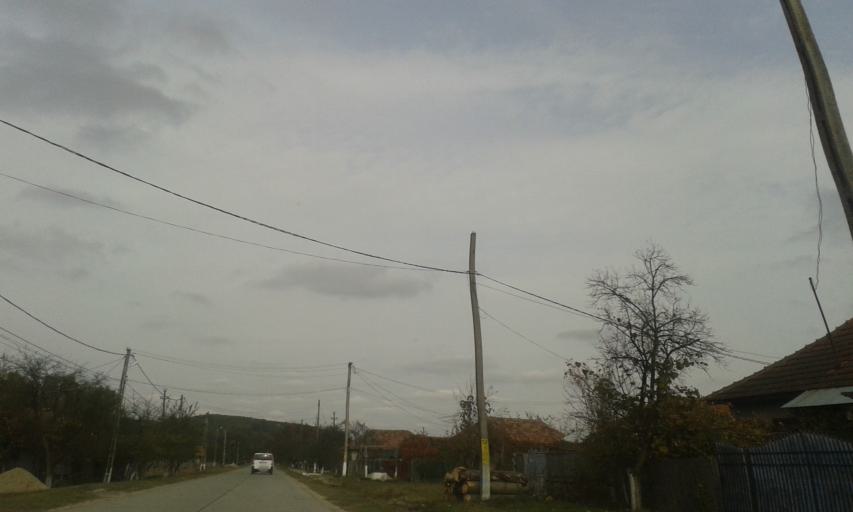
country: RO
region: Gorj
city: Logresti
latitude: 44.8790
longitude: 23.7103
